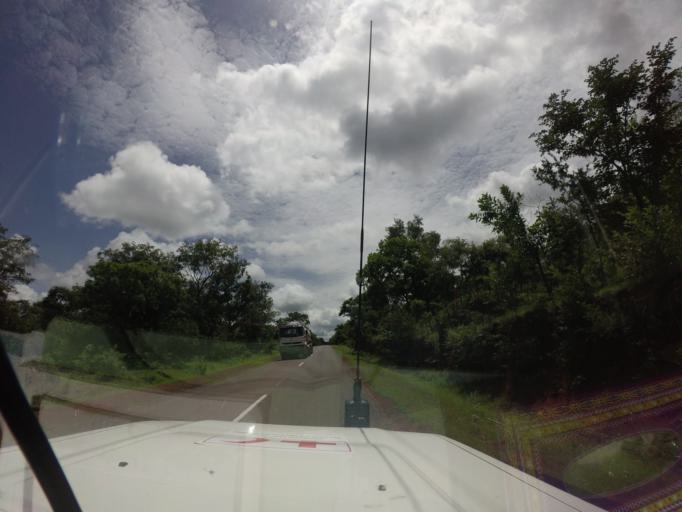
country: SL
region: Northern Province
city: Gberia Fotombu
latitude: 10.0885
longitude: -11.1356
